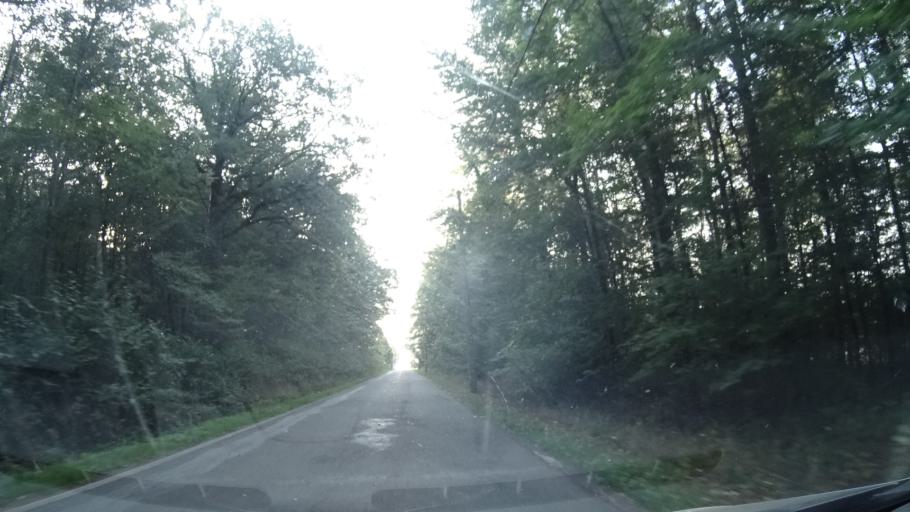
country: BE
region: Wallonia
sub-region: Province du Hainaut
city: Froidchapelle
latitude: 50.2147
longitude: 4.3460
